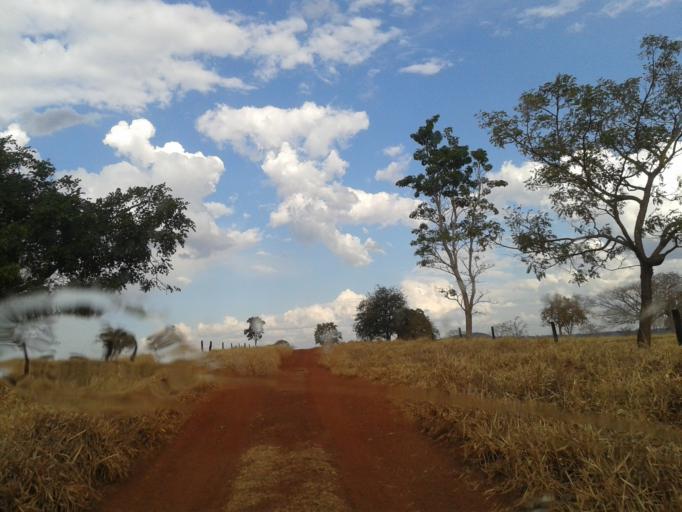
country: BR
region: Minas Gerais
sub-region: Santa Vitoria
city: Santa Vitoria
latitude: -19.1773
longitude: -49.9849
